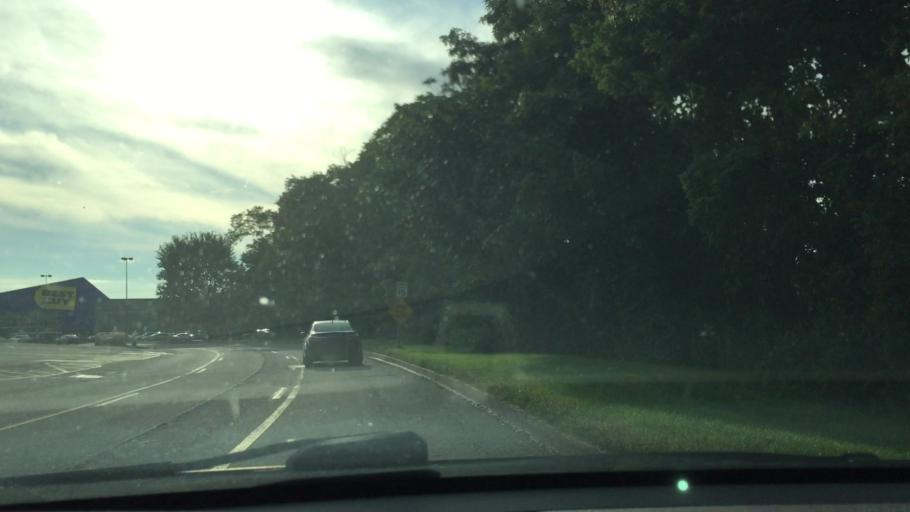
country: US
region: Pennsylvania
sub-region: Allegheny County
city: Monroeville
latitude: 40.4316
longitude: -79.7973
